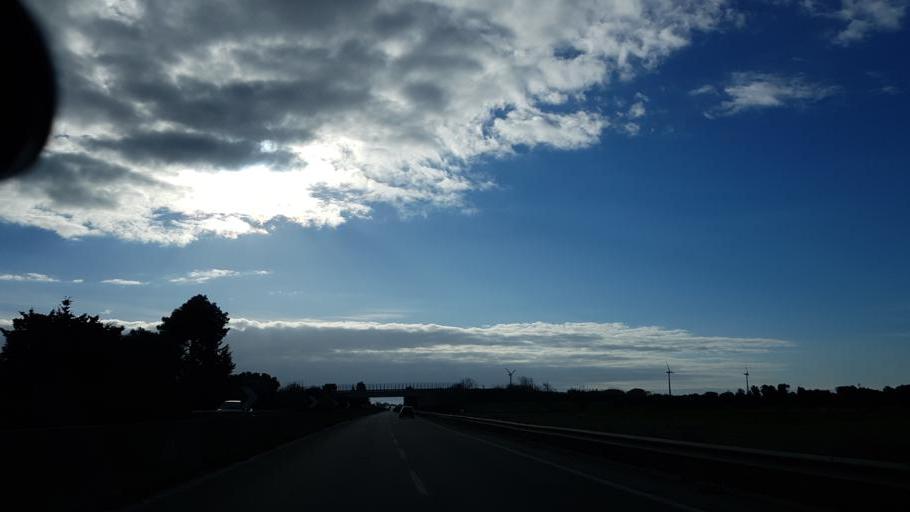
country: IT
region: Apulia
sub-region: Provincia di Brindisi
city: La Rosa
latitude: 40.5788
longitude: 17.9792
